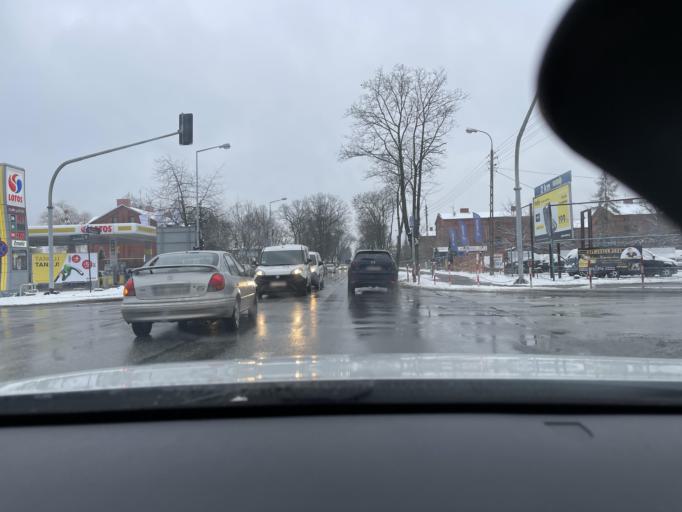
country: PL
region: Masovian Voivodeship
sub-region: Powiat zyrardowski
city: Zyrardow
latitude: 52.0488
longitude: 20.4458
